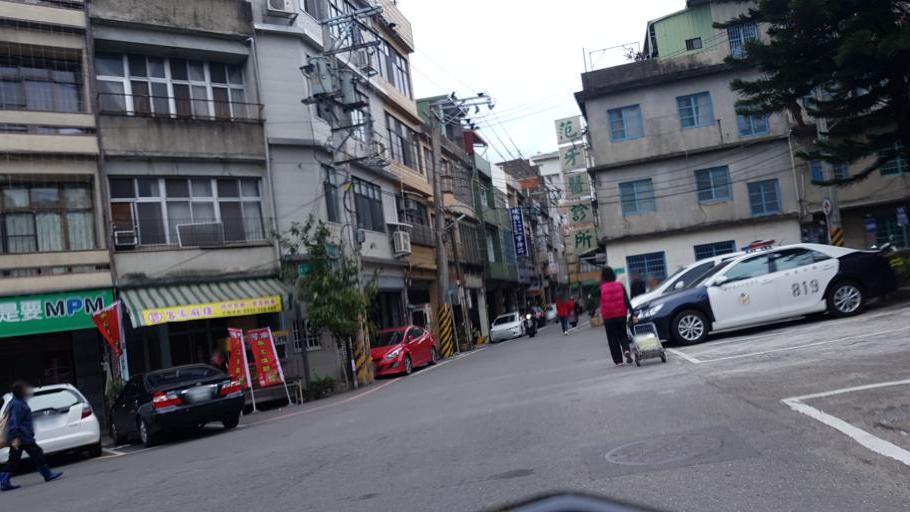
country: TW
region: Taiwan
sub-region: Hsinchu
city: Zhubei
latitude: 24.7374
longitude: 121.0869
